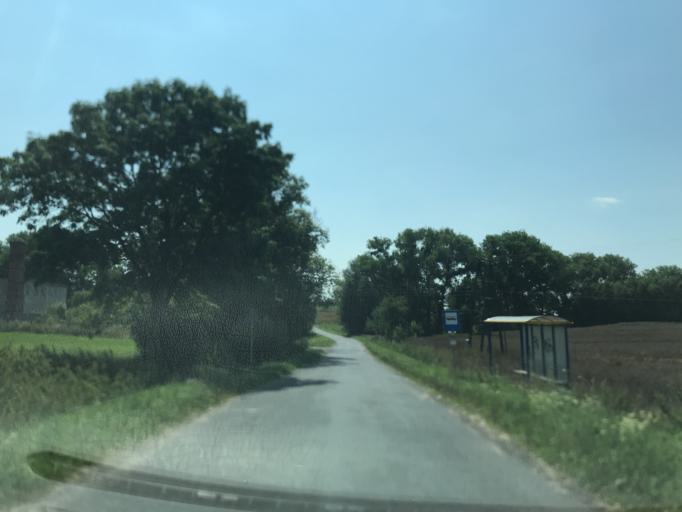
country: PL
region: Kujawsko-Pomorskie
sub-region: Powiat golubsko-dobrzynski
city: Zbojno
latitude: 52.9821
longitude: 19.2074
